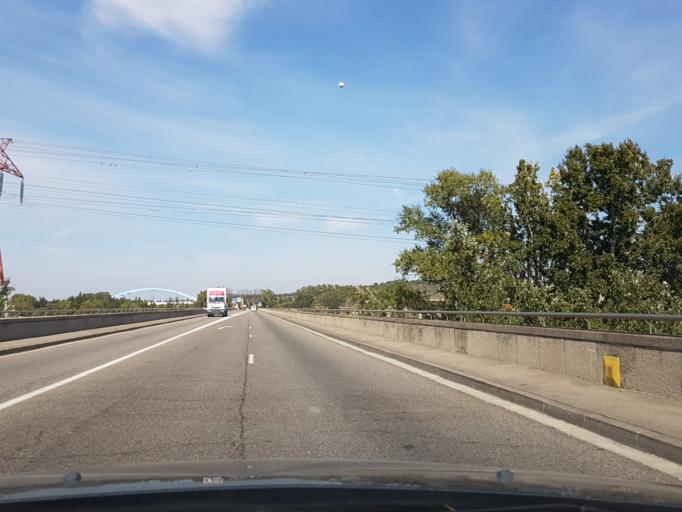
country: FR
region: Provence-Alpes-Cote d'Azur
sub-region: Departement des Bouches-du-Rhone
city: Noves
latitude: 43.8849
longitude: 4.9162
